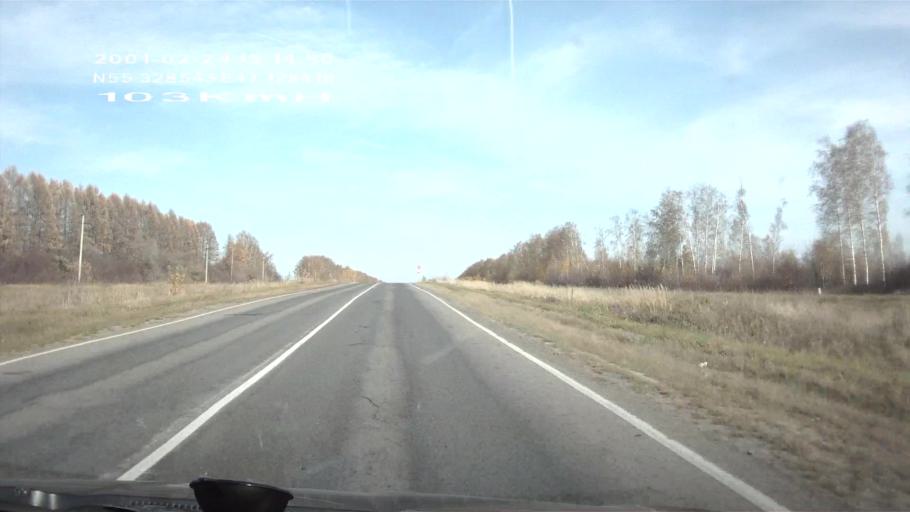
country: RU
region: Chuvashia
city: Ibresi
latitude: 55.3287
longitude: 47.1290
